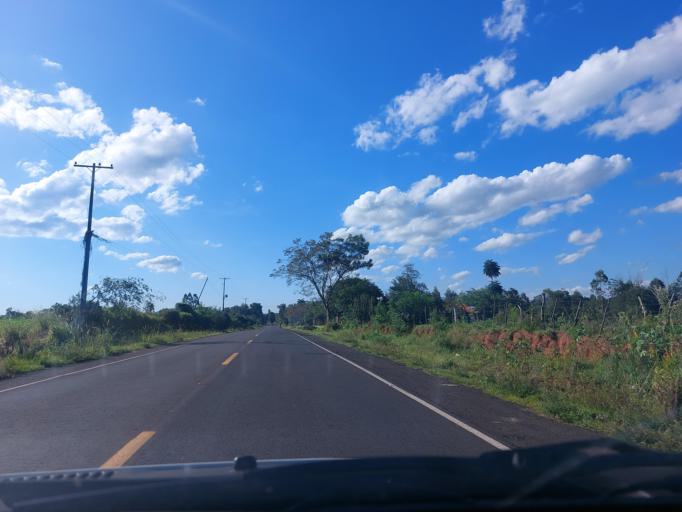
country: PY
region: San Pedro
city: Guayaybi
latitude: -24.5732
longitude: -56.5195
